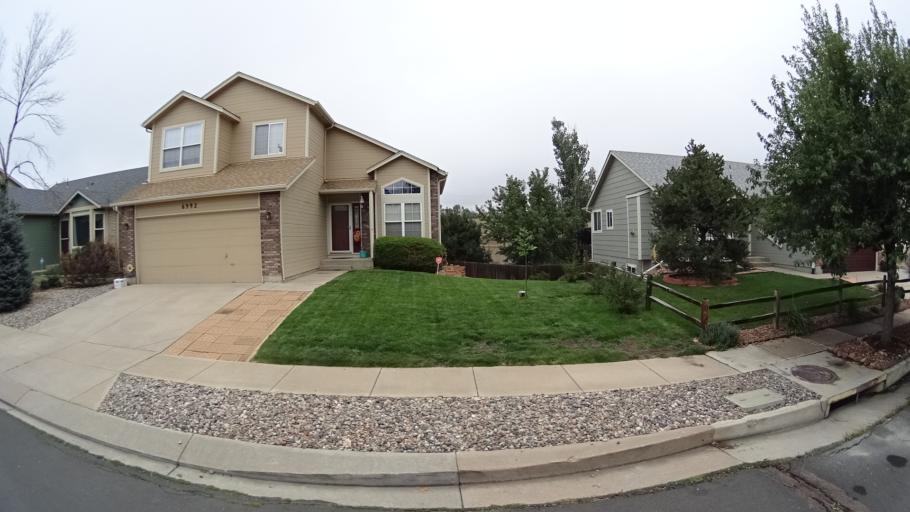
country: US
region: Colorado
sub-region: El Paso County
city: Black Forest
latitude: 38.9378
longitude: -104.7426
